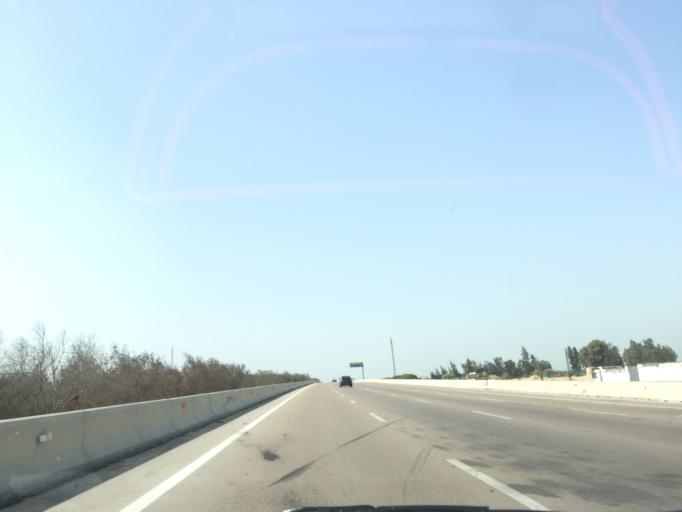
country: EG
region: Al Buhayrah
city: Beheira
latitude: 30.5436
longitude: 30.2096
